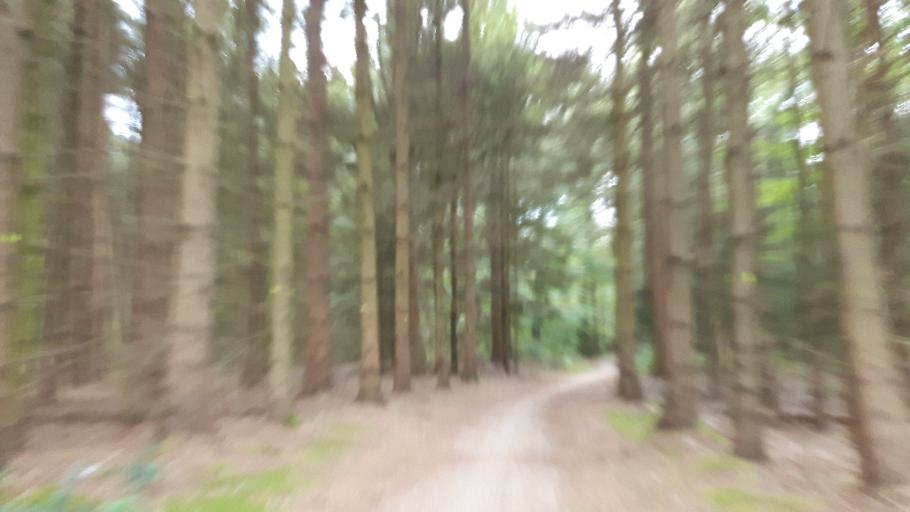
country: NL
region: Friesland
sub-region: Gemeente Smallingerland
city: Drachtstercompagnie
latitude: 53.0723
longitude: 6.2110
